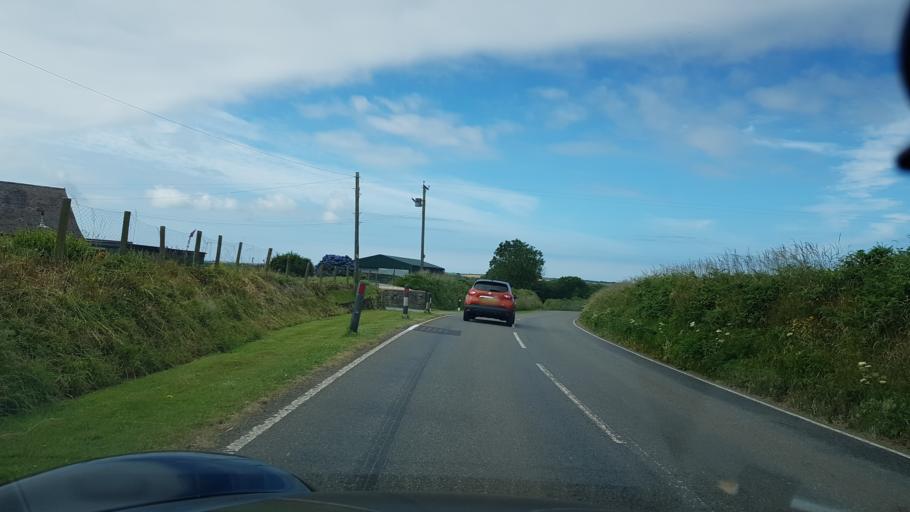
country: GB
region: Wales
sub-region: Pembrokeshire
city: Herbrandston
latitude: 51.7697
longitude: -5.0640
